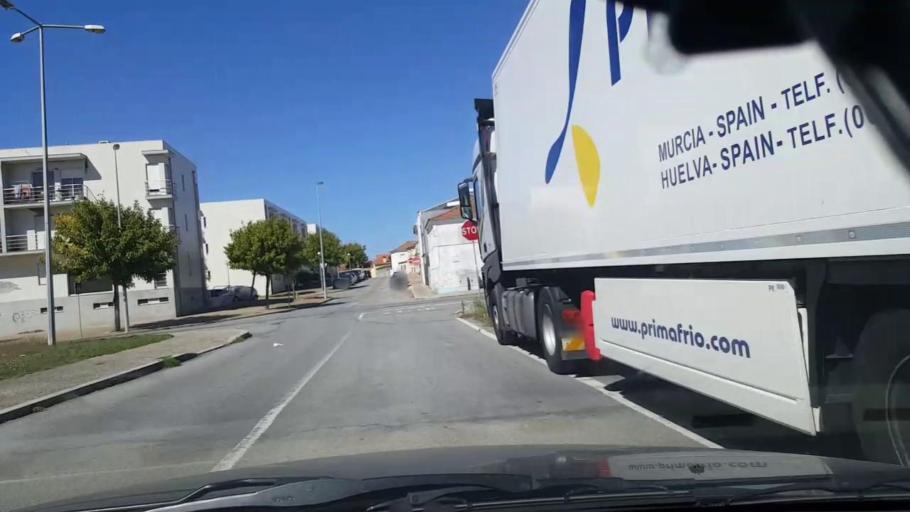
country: PT
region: Porto
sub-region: Vila do Conde
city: Arvore
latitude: 41.3428
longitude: -8.7320
